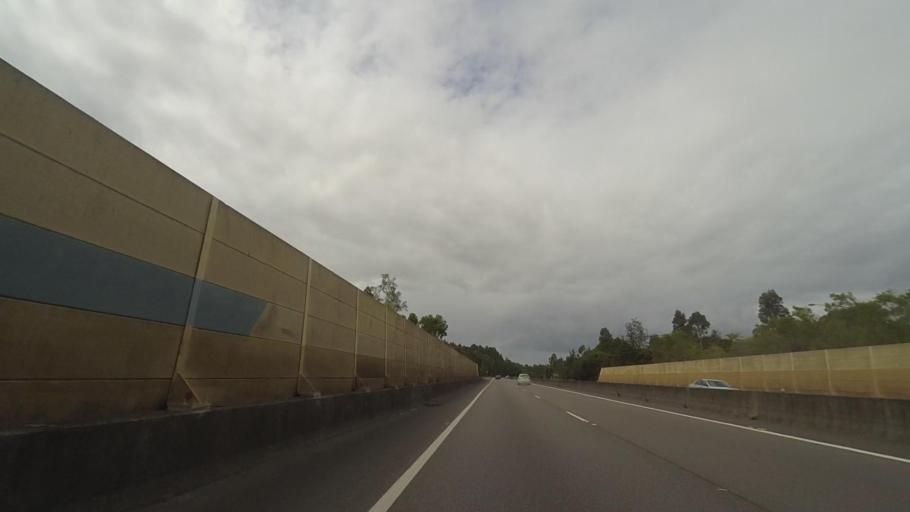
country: AU
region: New South Wales
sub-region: Port Stephens Shire
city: Raymond Terrace
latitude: -32.7537
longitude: 151.7659
